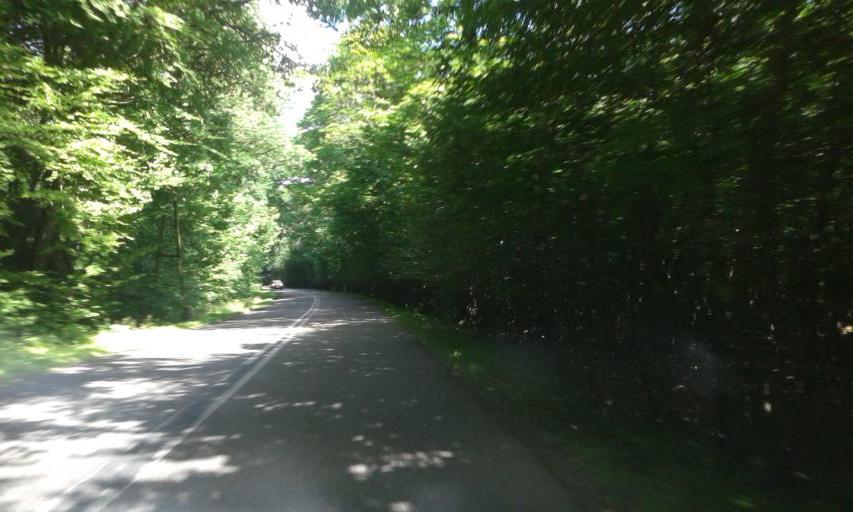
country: PL
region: West Pomeranian Voivodeship
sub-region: Powiat slawienski
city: Slawno
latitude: 54.2604
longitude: 16.6811
